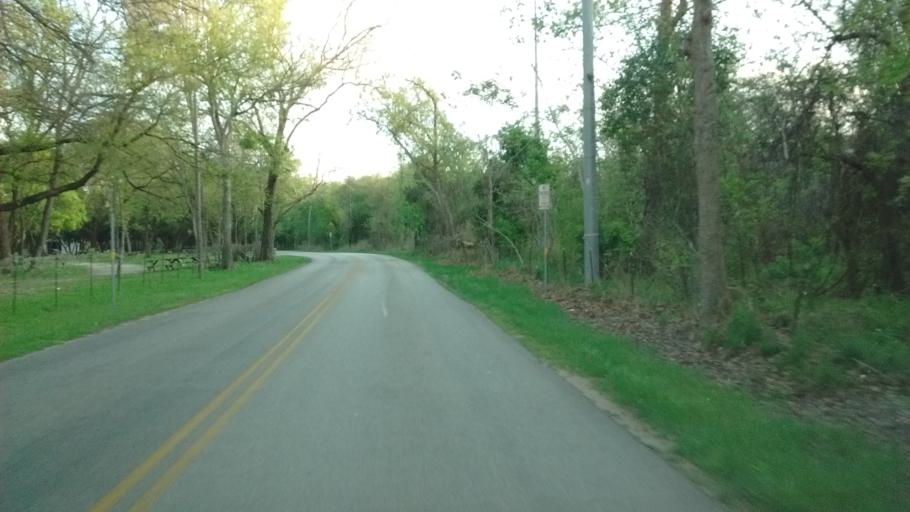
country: US
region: Texas
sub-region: Comal County
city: New Braunfels
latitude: 29.7597
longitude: -98.1403
